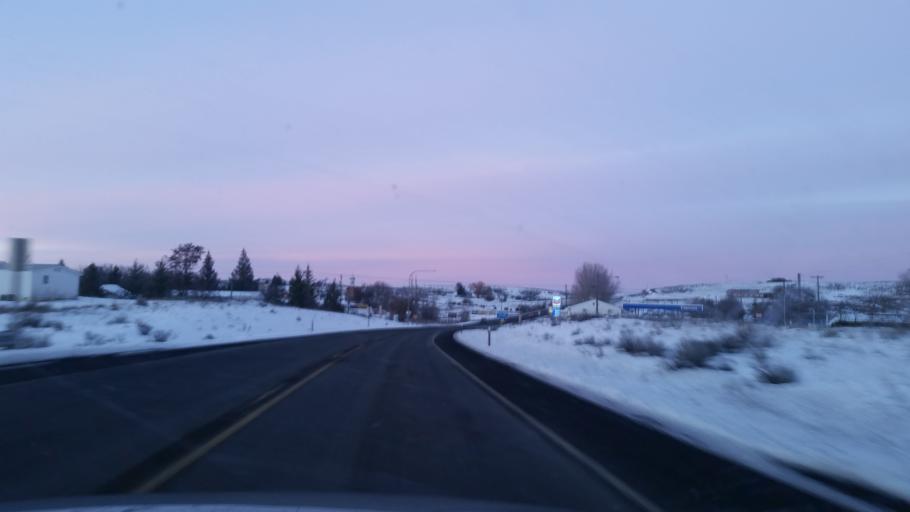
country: US
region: Washington
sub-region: Lincoln County
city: Davenport
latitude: 47.2962
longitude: -117.9736
